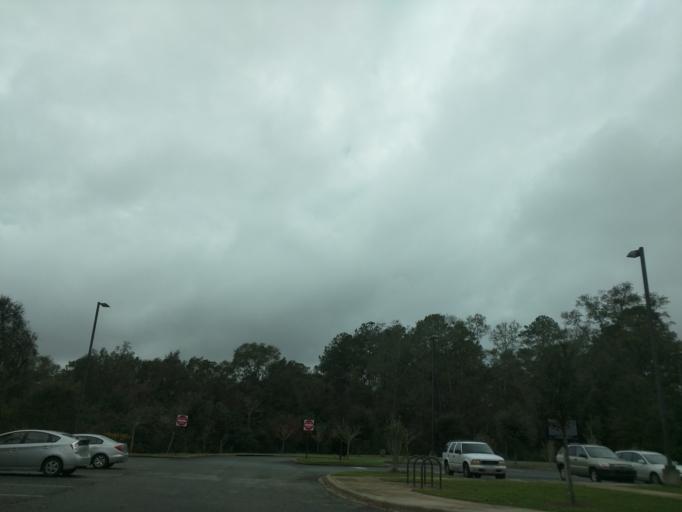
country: US
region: Florida
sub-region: Leon County
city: Tallahassee
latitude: 30.4485
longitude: -84.3203
